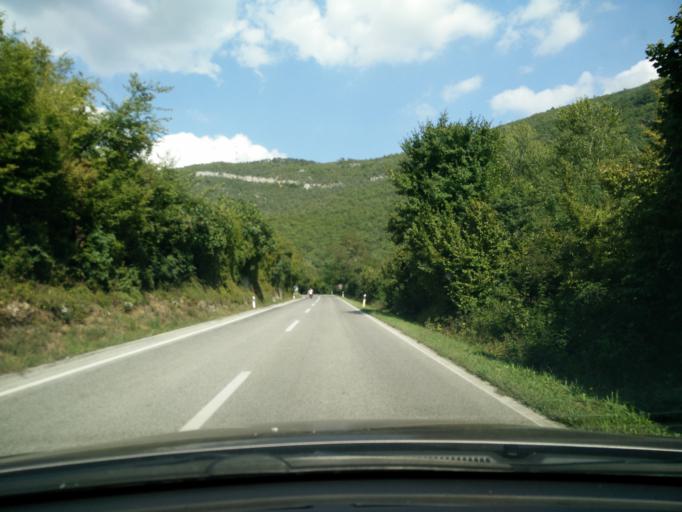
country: HR
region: Istarska
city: Buzet
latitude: 45.3806
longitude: 13.8929
